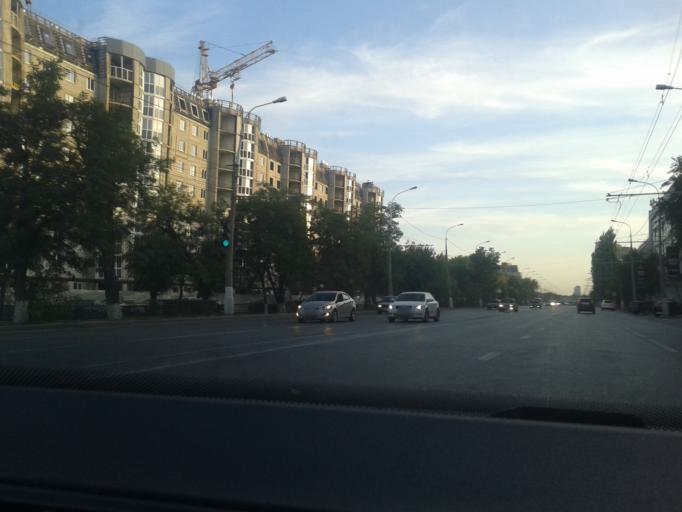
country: RU
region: Volgograd
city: Volgograd
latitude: 48.7341
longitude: 44.5426
